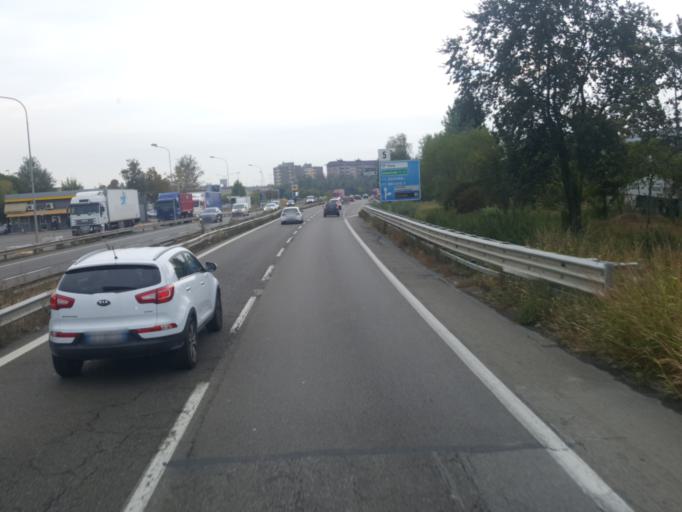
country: IT
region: Emilia-Romagna
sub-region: Provincia di Modena
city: Modena
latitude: 44.6513
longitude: 10.9605
